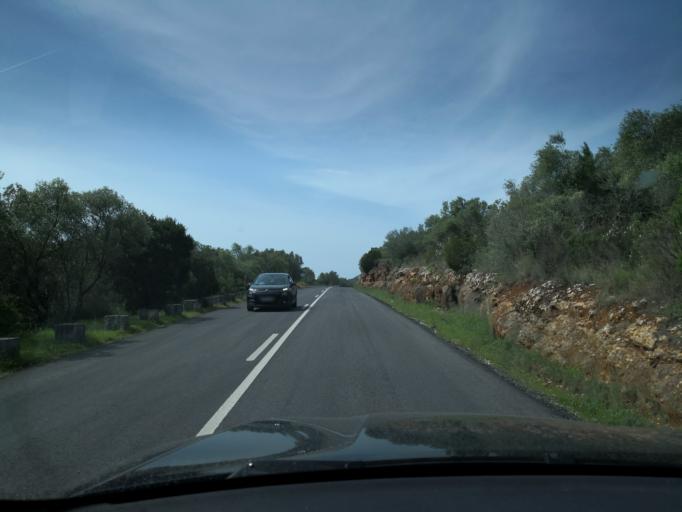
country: PT
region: Setubal
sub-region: Palmela
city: Quinta do Anjo
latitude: 38.4824
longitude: -8.9800
